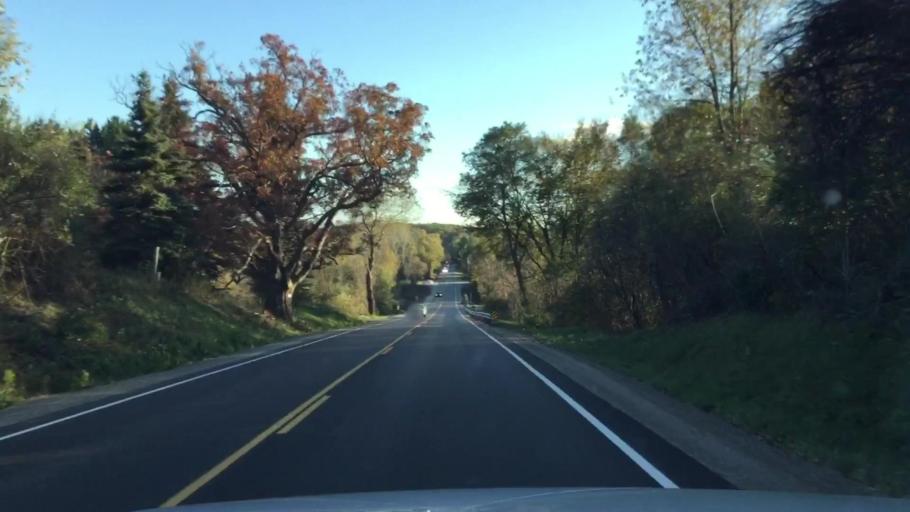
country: US
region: Michigan
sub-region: Lapeer County
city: Almont
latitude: 42.9056
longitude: -83.1428
